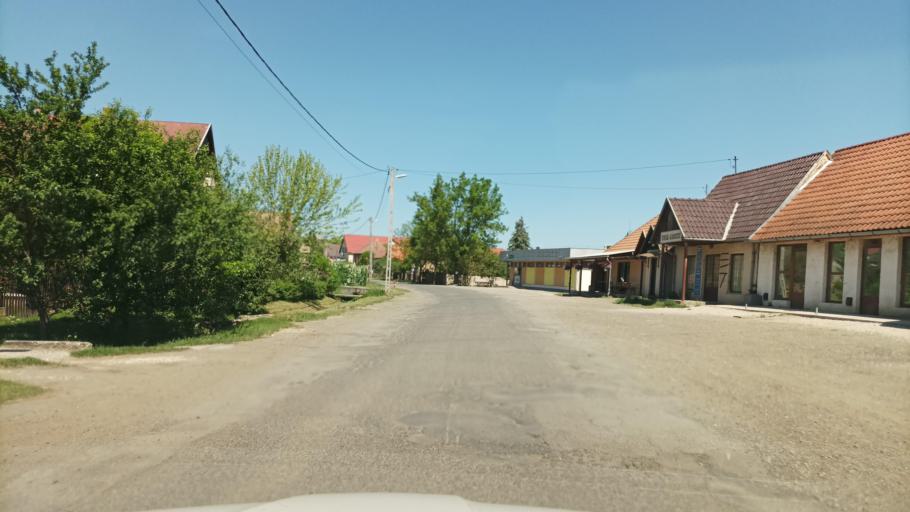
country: HU
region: Pest
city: Acsa
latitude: 47.7954
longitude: 19.3836
